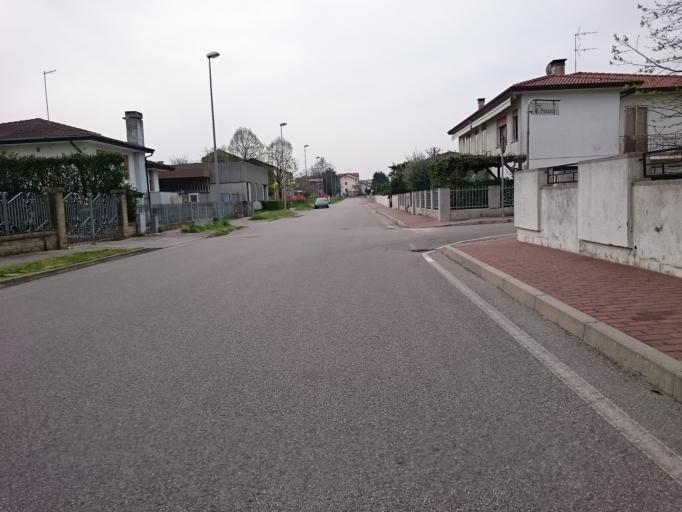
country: IT
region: Veneto
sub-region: Provincia di Padova
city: Bagnoli di Sopra
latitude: 45.1893
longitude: 11.8843
